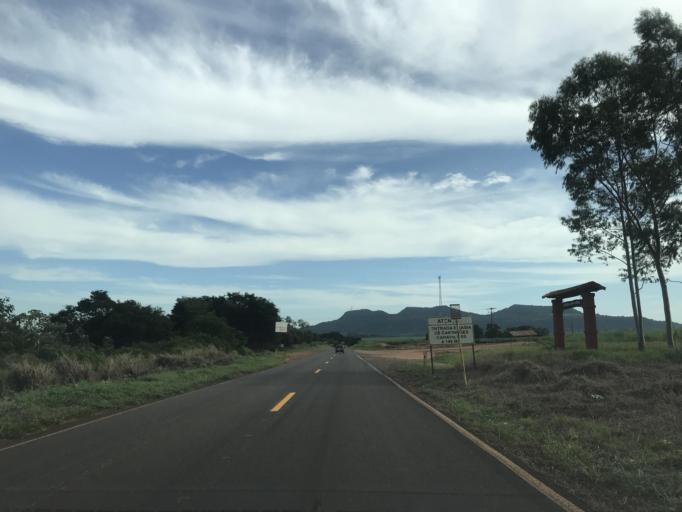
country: BR
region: Parana
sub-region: Paranavai
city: Nova Aurora
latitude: -22.8215
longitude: -52.6551
